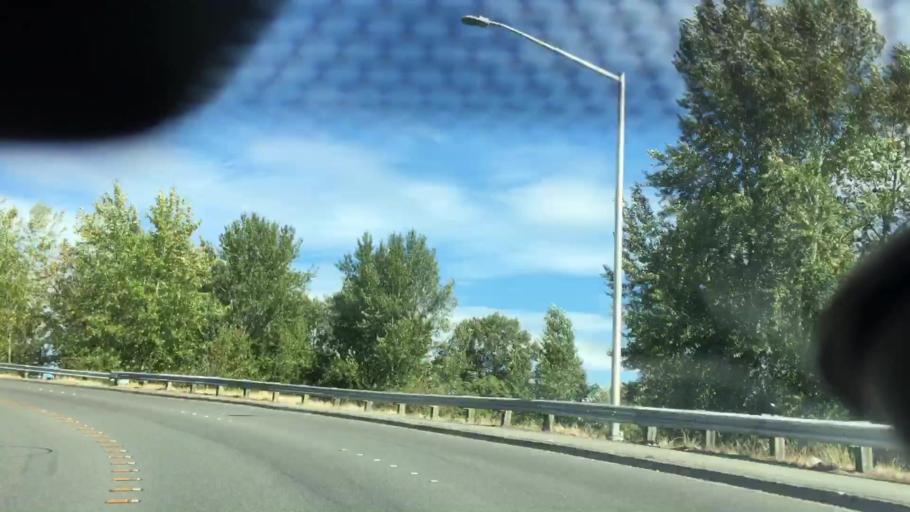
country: US
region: Washington
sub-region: King County
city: Tukwila
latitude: 47.4613
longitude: -122.2505
